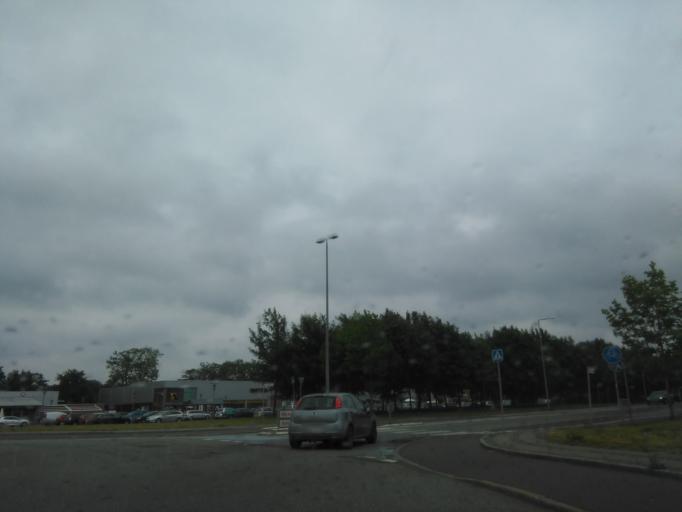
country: DK
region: Capital Region
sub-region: Bornholm Kommune
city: Ronne
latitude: 55.0925
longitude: 14.7285
